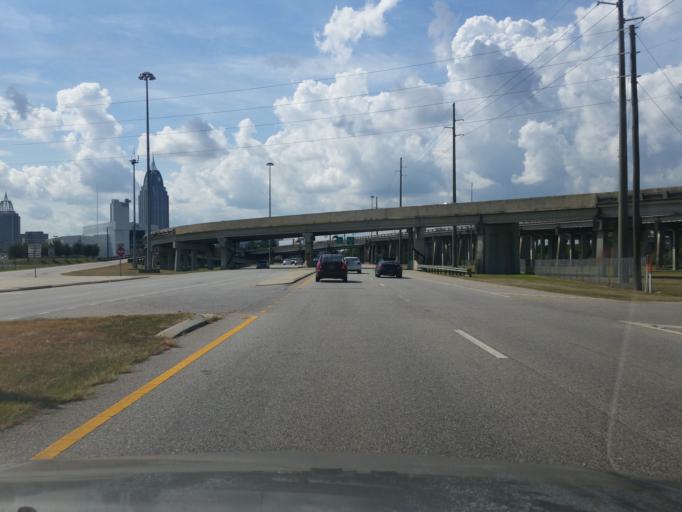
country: US
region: Alabama
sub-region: Mobile County
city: Mobile
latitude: 30.6908
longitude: -88.0244
